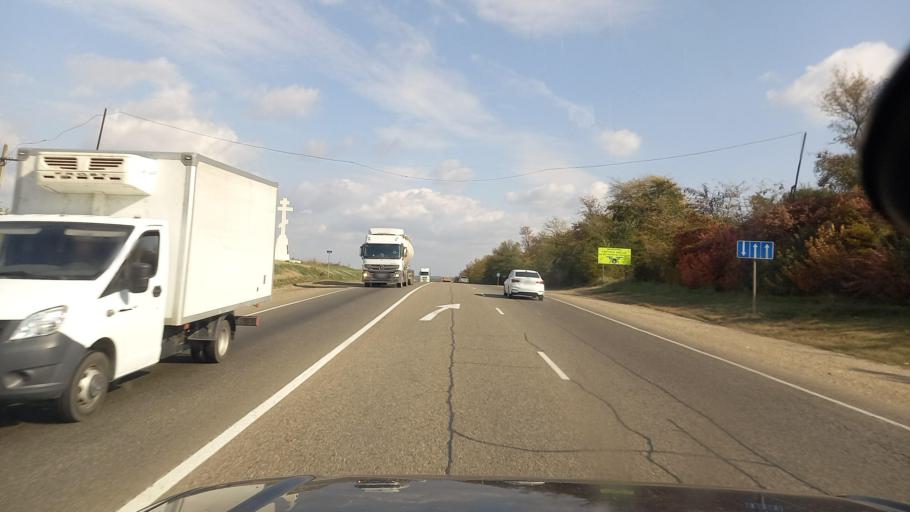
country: RU
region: Krasnodarskiy
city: Akhtyrskiy
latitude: 44.8475
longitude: 38.3136
